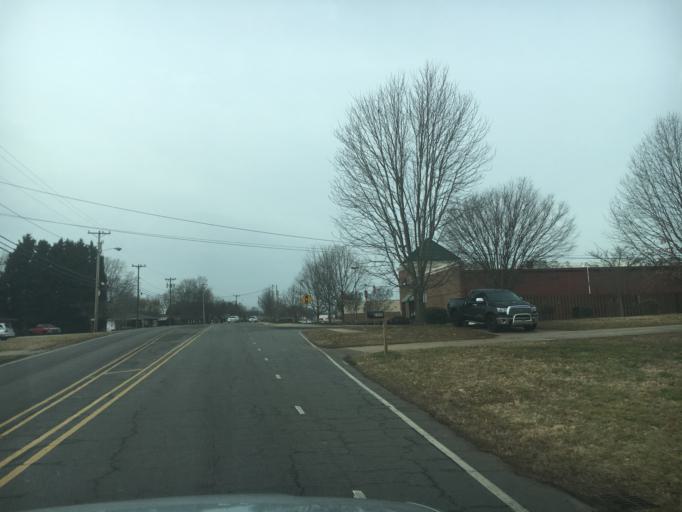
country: US
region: North Carolina
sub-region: Iredell County
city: Statesville
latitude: 35.7911
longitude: -80.8497
